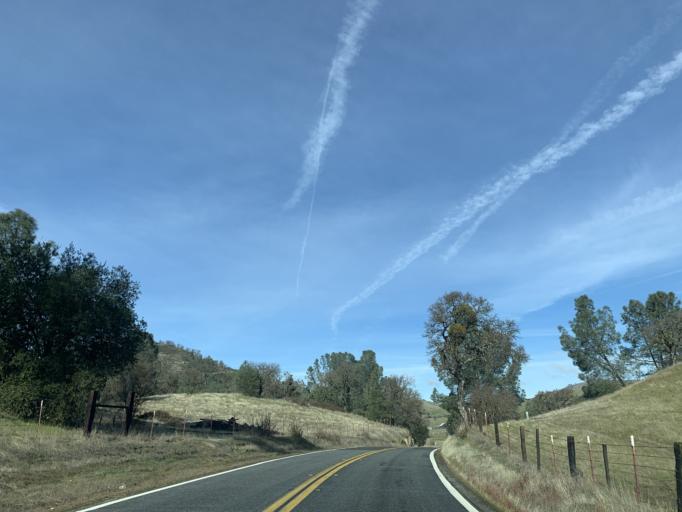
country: US
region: California
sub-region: Monterey County
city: Soledad
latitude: 36.5424
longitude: -121.1554
